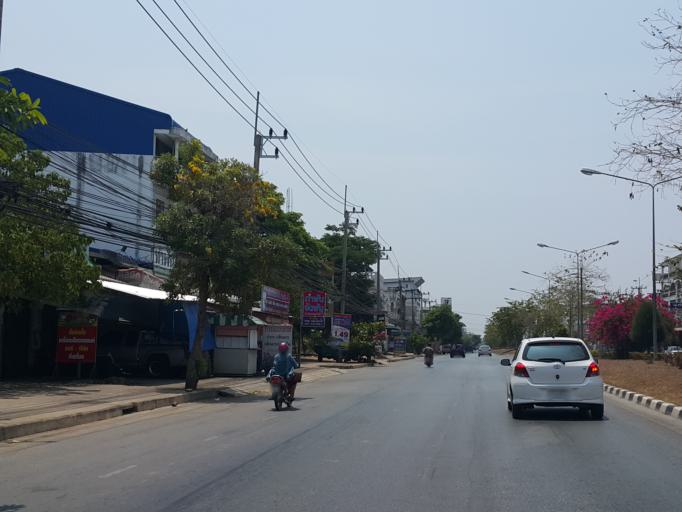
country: TH
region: Kanchanaburi
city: Kanchanaburi
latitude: 14.0405
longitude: 99.5162
